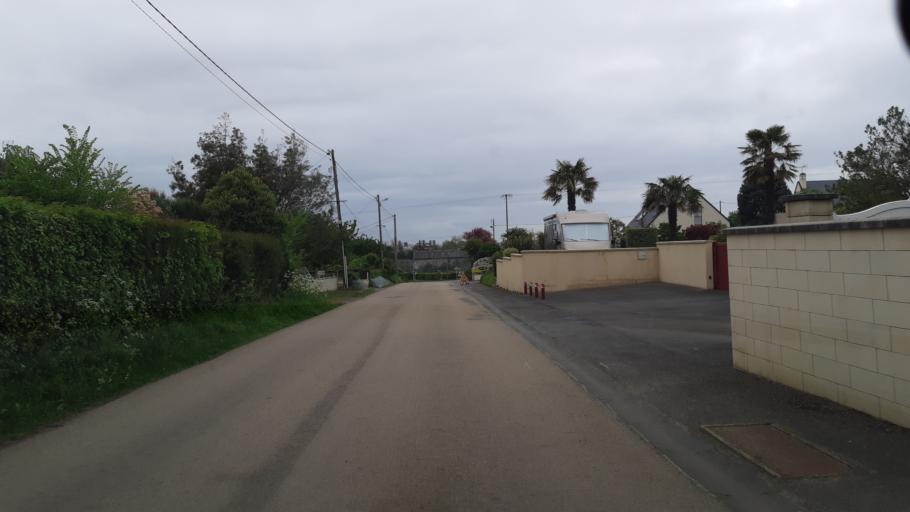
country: FR
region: Lower Normandy
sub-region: Departement de la Manche
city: Donville-les-Bains
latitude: 48.8560
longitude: -1.5489
